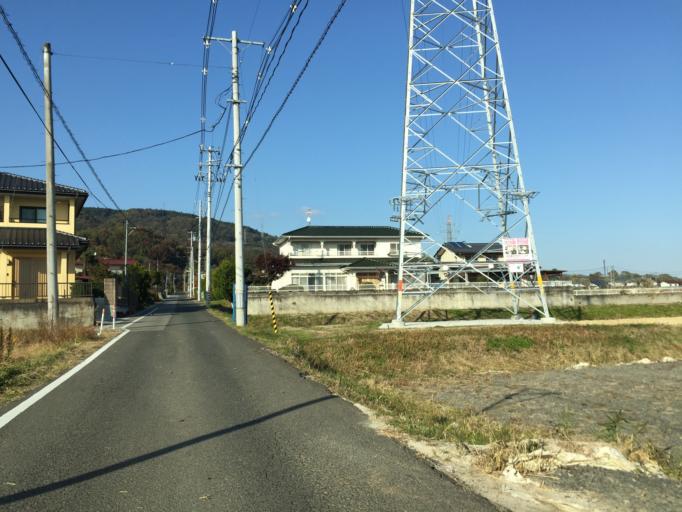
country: JP
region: Fukushima
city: Hobaramachi
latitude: 37.8330
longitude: 140.4942
